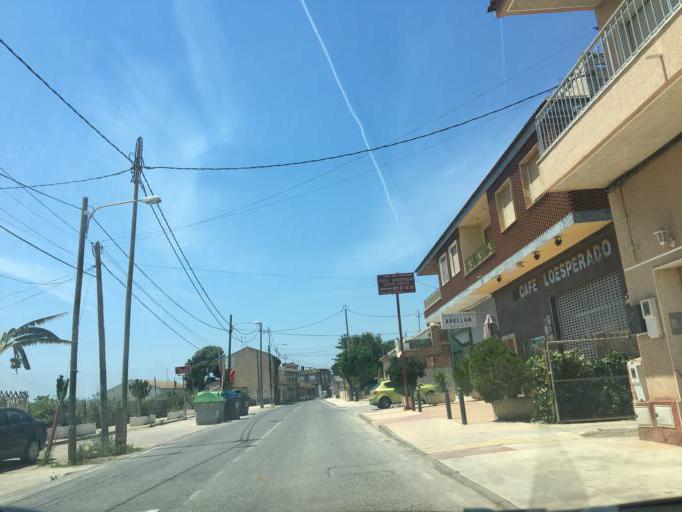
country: ES
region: Murcia
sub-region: Murcia
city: Santomera
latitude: 38.0339
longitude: -1.0596
